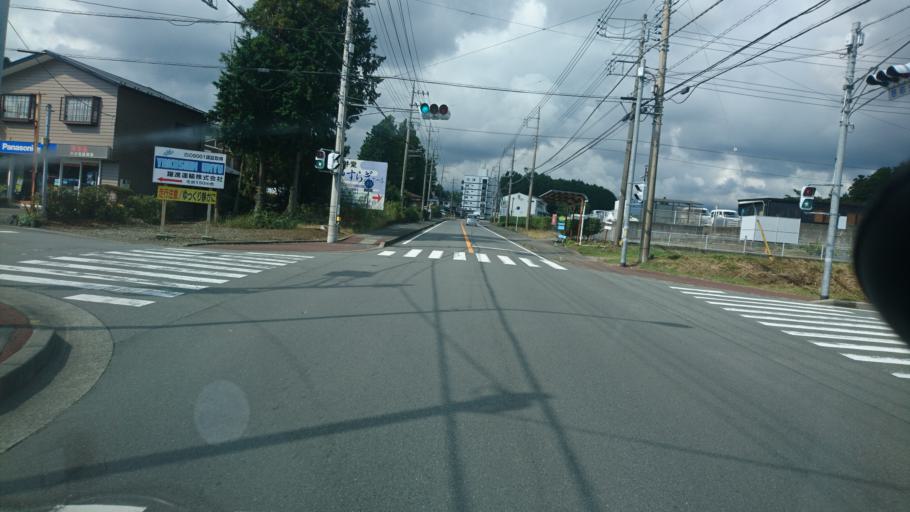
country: JP
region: Shizuoka
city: Gotemba
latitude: 35.3080
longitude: 138.9134
